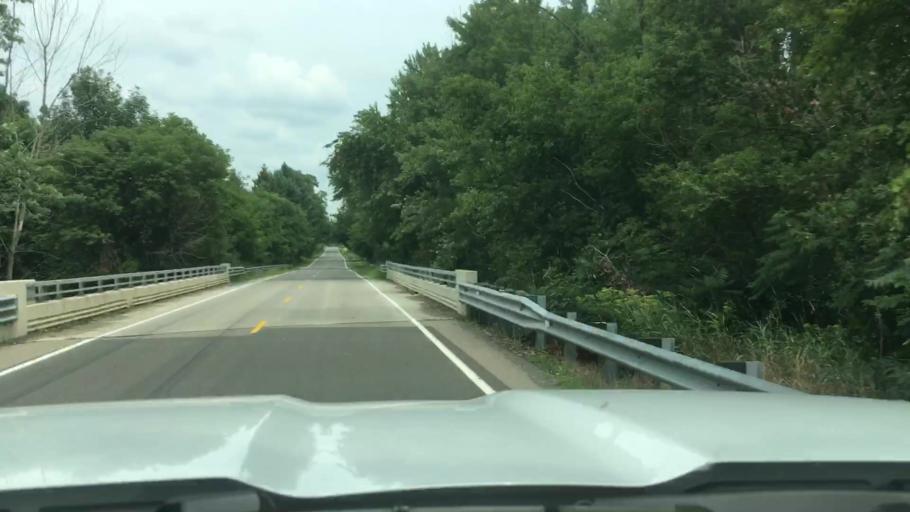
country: US
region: Michigan
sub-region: Ingham County
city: Webberville
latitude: 42.6812
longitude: -84.1895
